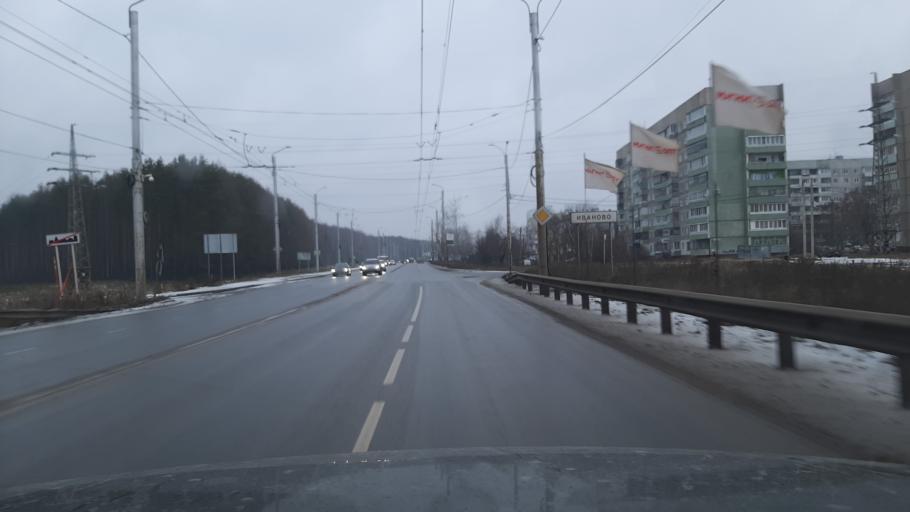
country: RU
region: Ivanovo
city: Kokhma
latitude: 56.9476
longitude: 41.0537
